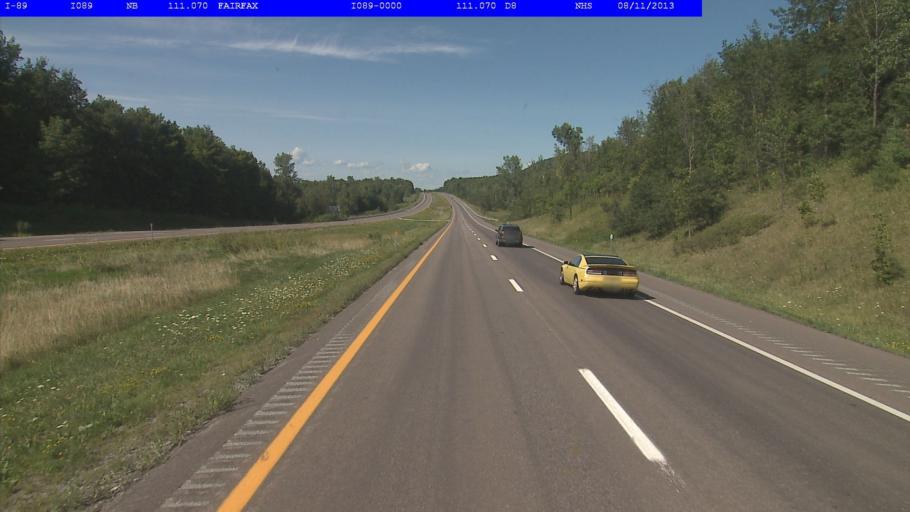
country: US
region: Vermont
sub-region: Franklin County
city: Saint Albans
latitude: 44.7566
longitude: -73.0770
